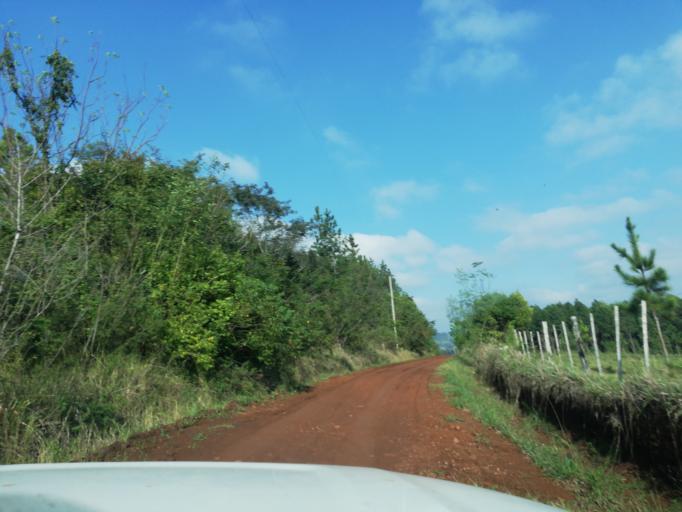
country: AR
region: Misiones
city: Cerro Azul
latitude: -27.5924
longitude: -55.5158
